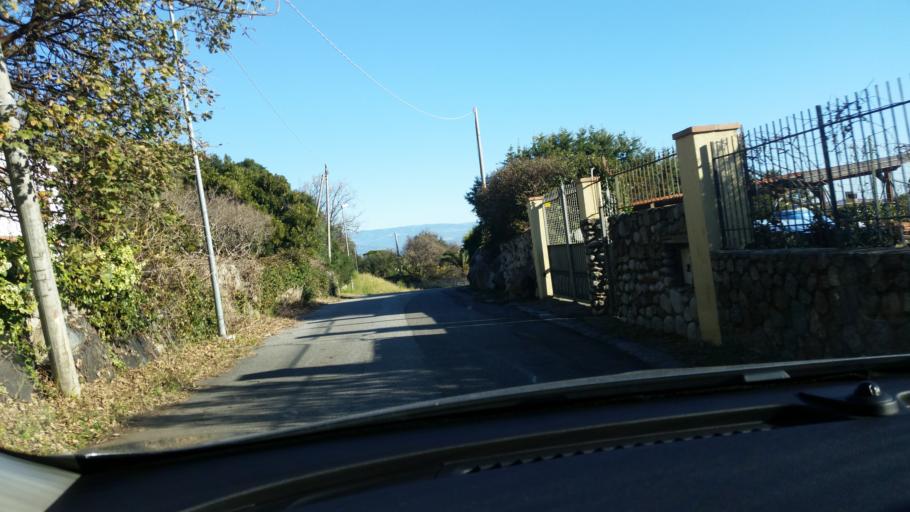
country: IT
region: Calabria
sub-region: Provincia di Catanzaro
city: Squillace Lido
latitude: 38.7601
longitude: 16.5672
